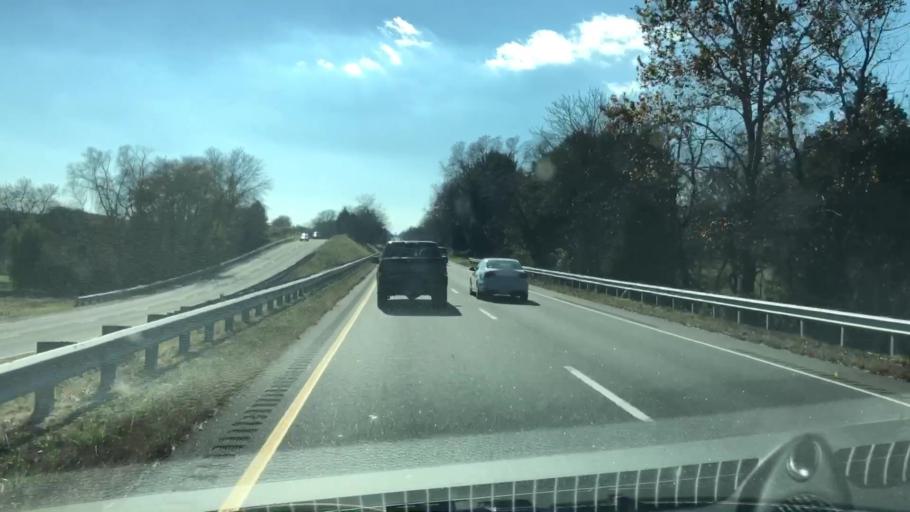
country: US
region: Virginia
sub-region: Madison County
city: Madison
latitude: 38.3409
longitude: -78.2906
